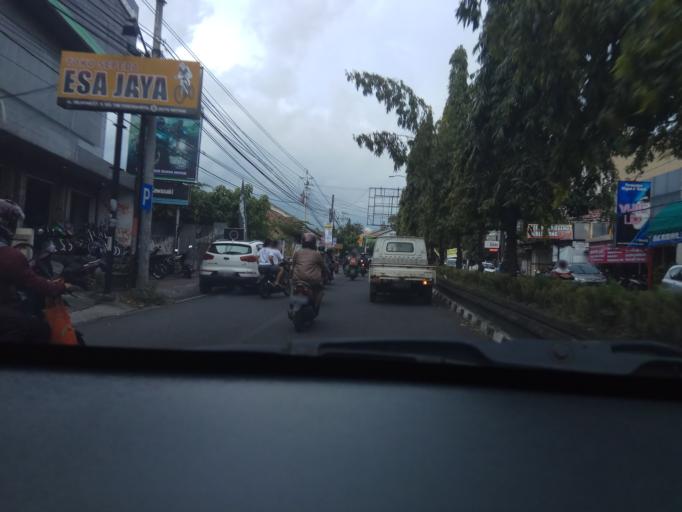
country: ID
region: Daerah Istimewa Yogyakarta
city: Yogyakarta
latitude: -7.7642
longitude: 110.3931
